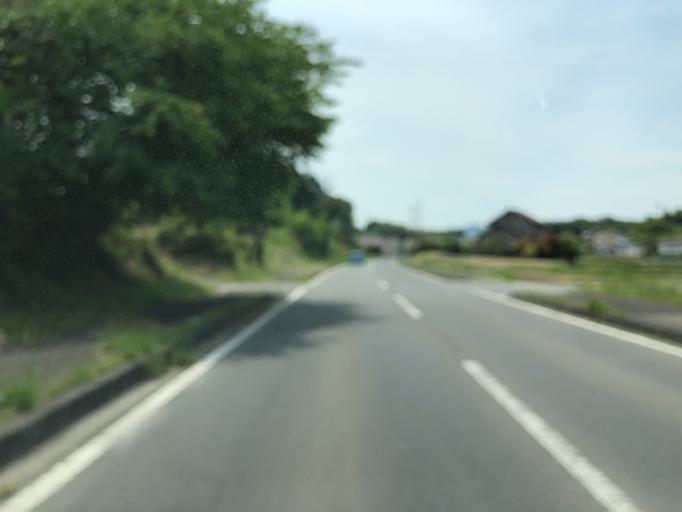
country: JP
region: Miyagi
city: Marumori
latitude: 37.8181
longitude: 140.9364
